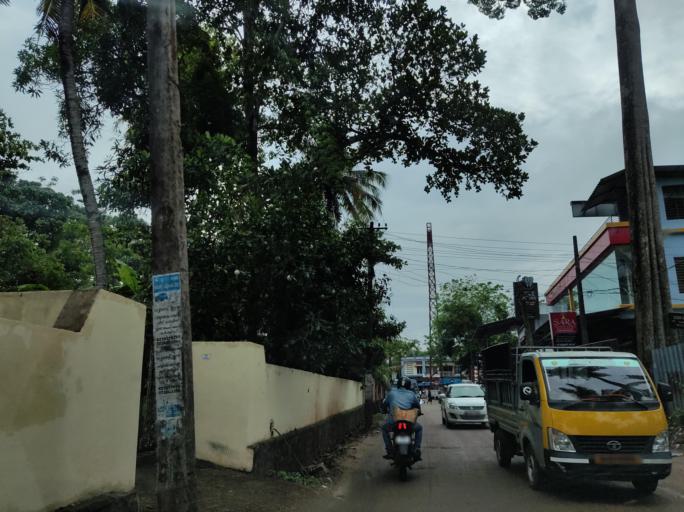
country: IN
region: Kerala
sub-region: Alappuzha
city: Mavelikara
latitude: 9.2418
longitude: 76.5206
